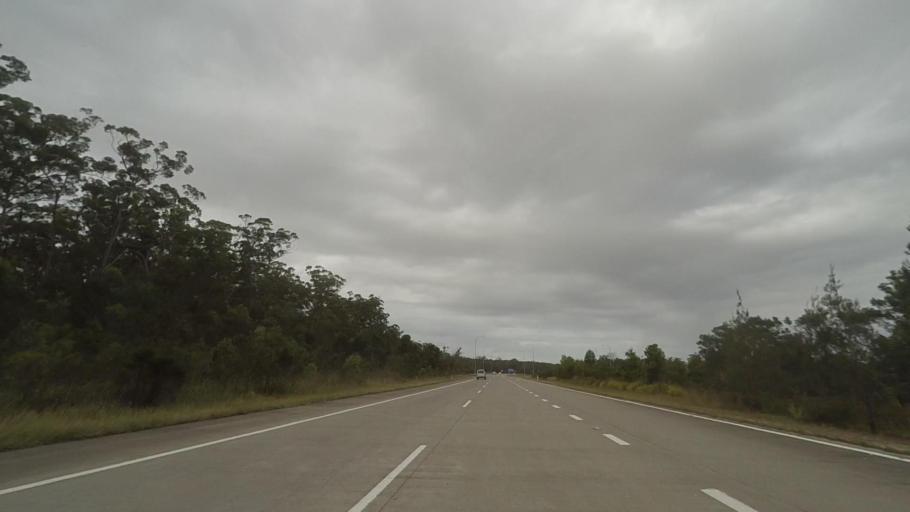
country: AU
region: New South Wales
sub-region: Port Stephens Shire
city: Port Stephens
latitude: -32.6149
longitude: 152.0772
